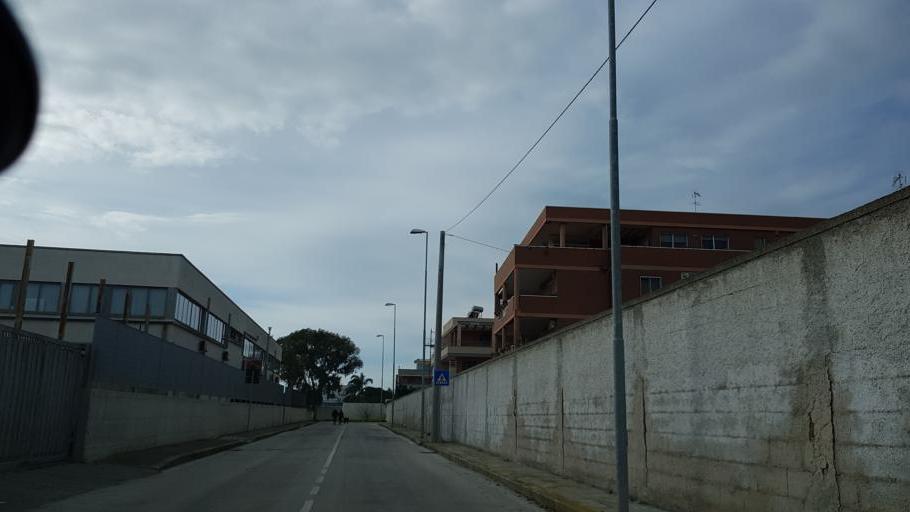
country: IT
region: Apulia
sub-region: Provincia di Brindisi
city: Materdomini
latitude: 40.6579
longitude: 17.9606
